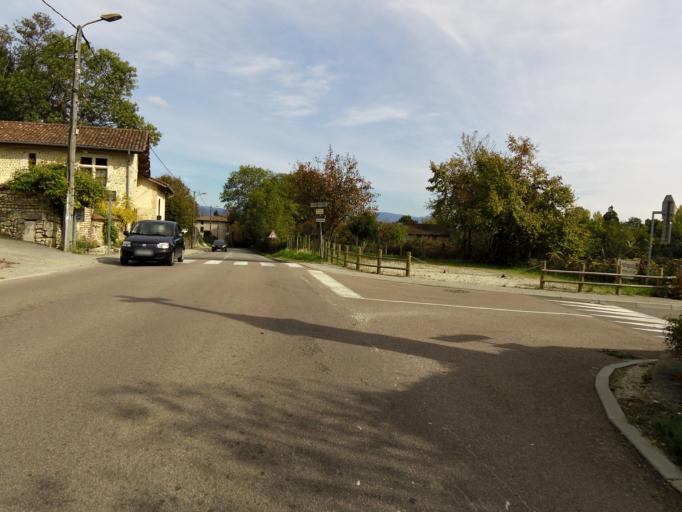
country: FR
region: Rhone-Alpes
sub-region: Departement de l'Ain
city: Perouges
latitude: 45.9017
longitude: 5.1813
